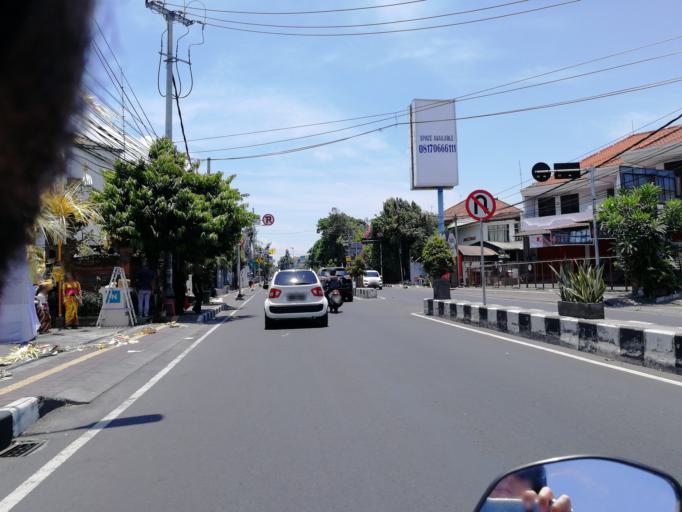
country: ID
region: Bali
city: Karyadharma
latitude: -8.6797
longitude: 115.2043
